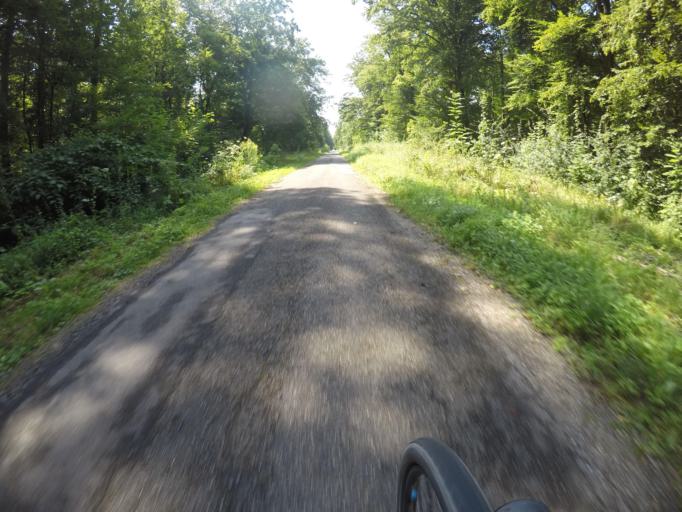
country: DE
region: Baden-Wuerttemberg
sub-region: Karlsruhe Region
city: Forst
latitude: 49.1806
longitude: 8.5970
